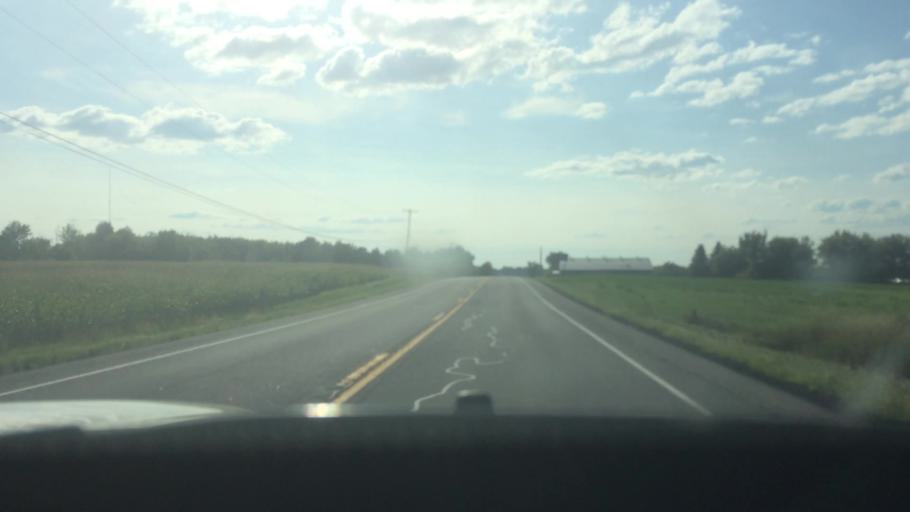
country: US
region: New York
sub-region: St. Lawrence County
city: Potsdam
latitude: 44.6890
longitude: -74.7203
